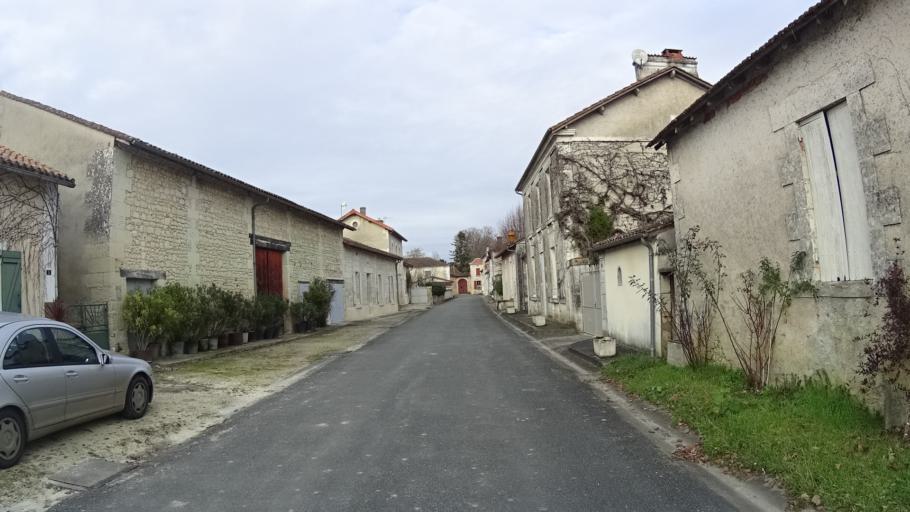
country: FR
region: Aquitaine
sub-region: Departement de la Dordogne
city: Saint-Aulaye
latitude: 45.2397
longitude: 0.1500
